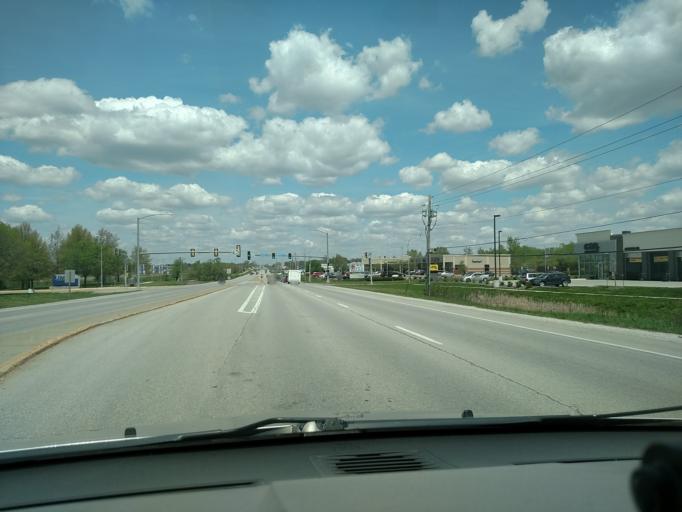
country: US
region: Iowa
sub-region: Polk County
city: Ankeny
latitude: 41.7079
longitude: -93.6005
